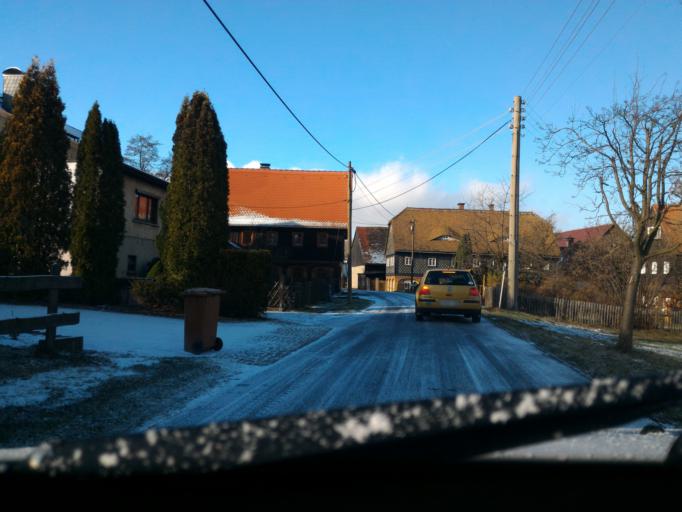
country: CZ
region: Ustecky
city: Varnsdorf
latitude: 50.8798
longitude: 14.6339
